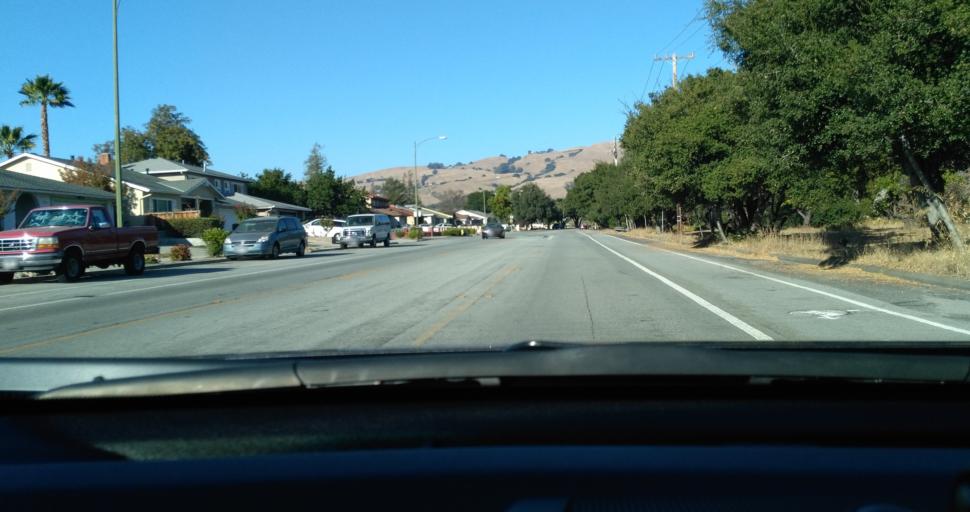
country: US
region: California
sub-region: Santa Clara County
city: Alum Rock
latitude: 37.3870
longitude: -121.8516
